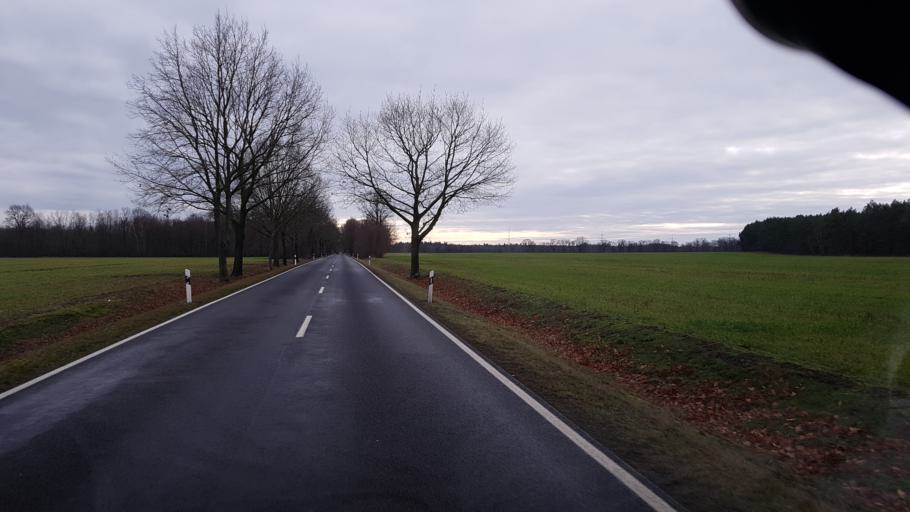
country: DE
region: Brandenburg
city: Altdobern
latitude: 51.6806
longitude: 14.0274
